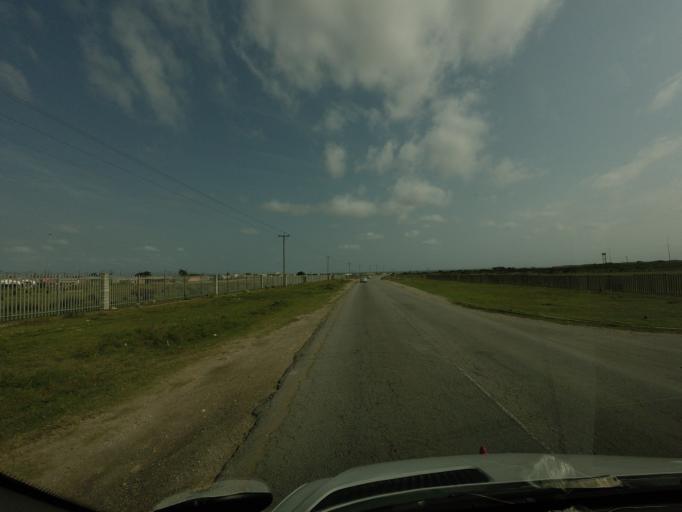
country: ZA
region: Eastern Cape
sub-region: Nelson Mandela Bay Metropolitan Municipality
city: Port Elizabeth
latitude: -33.7832
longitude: 25.5916
